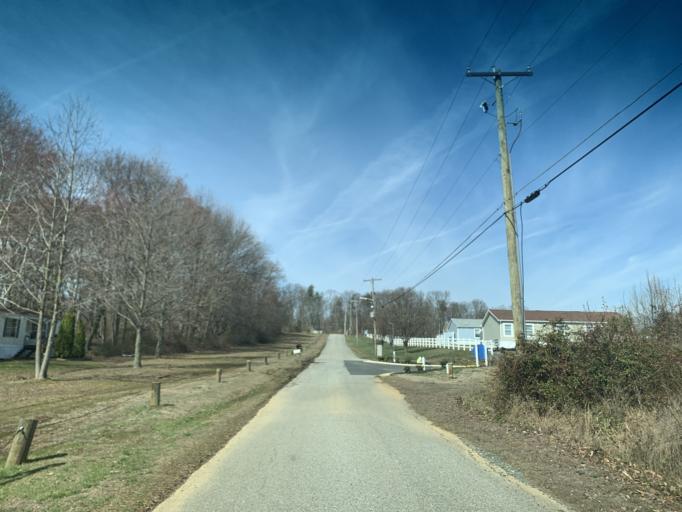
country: US
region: Maryland
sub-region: Cecil County
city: Charlestown
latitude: 39.5541
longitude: -76.0091
